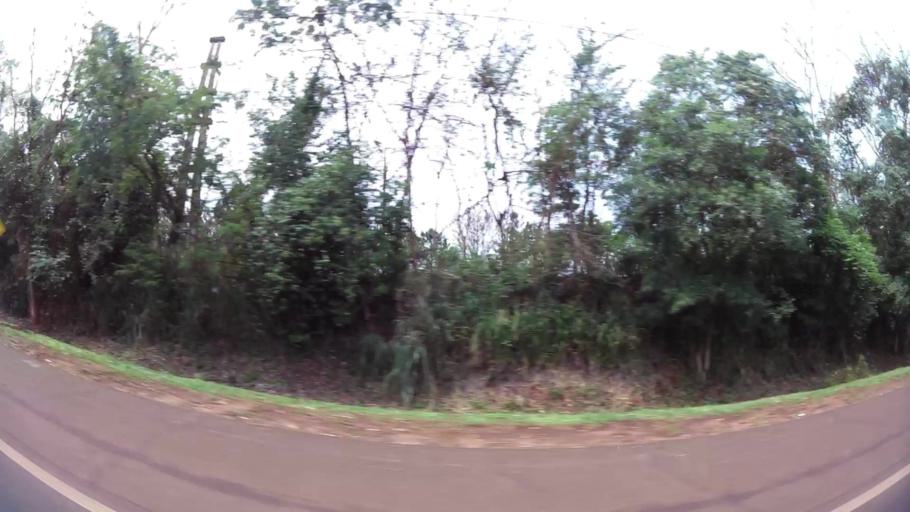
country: PY
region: Alto Parana
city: Ciudad del Este
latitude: -25.4867
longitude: -54.6286
